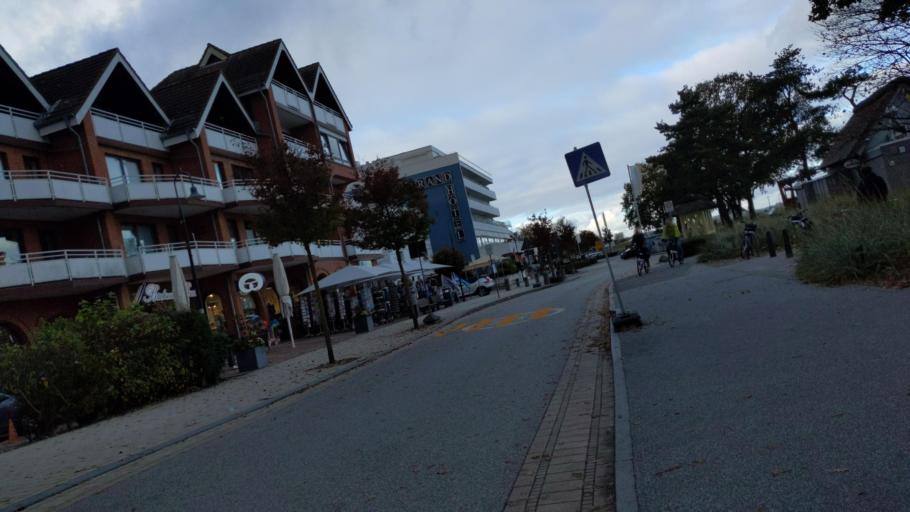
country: DE
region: Schleswig-Holstein
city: Scharbeutz
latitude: 54.0288
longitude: 10.7560
